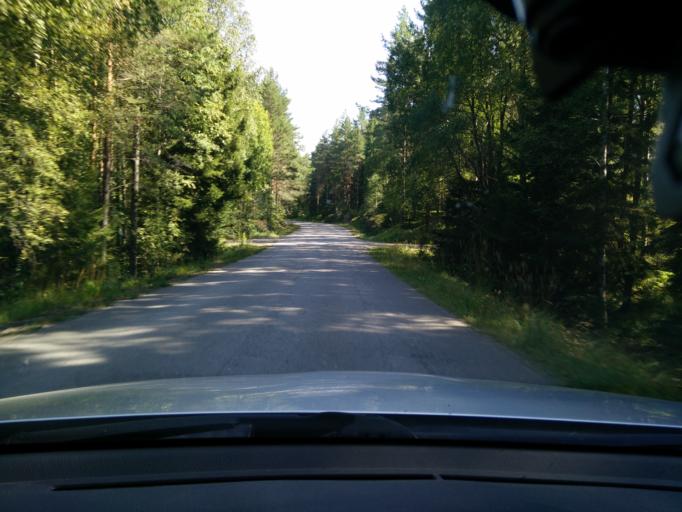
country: SE
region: OEstergoetland
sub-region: Norrkopings Kommun
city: Jursla
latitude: 58.7196
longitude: 16.1389
